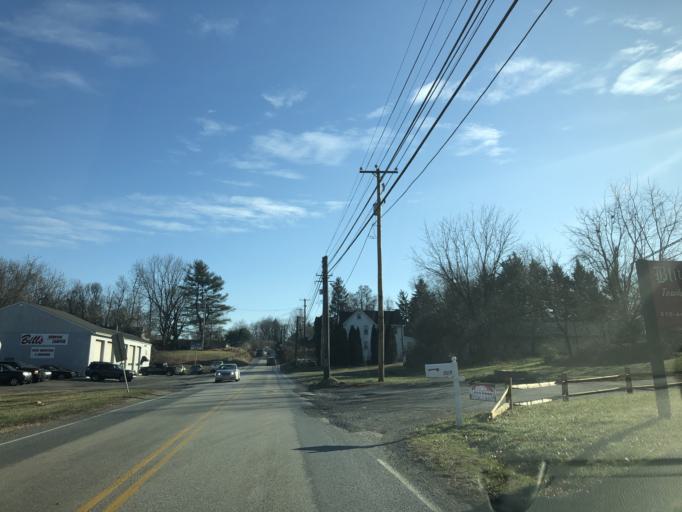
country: US
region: Pennsylvania
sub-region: Chester County
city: Toughkenamon
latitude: 39.8254
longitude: -75.7552
